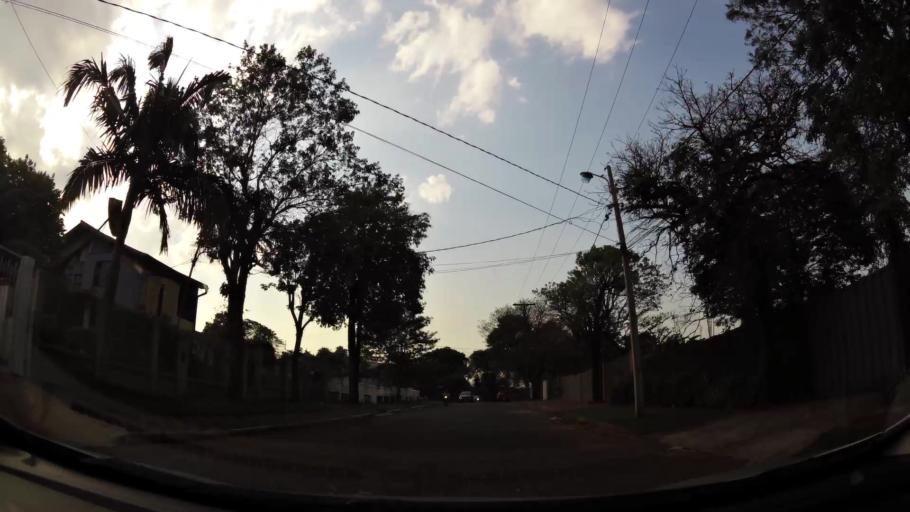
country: PY
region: Alto Parana
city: Presidente Franco
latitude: -25.5186
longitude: -54.6397
